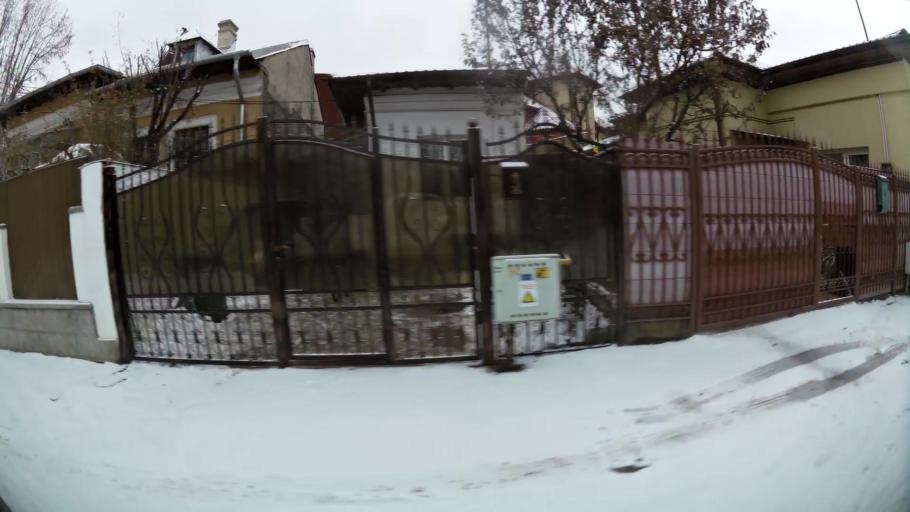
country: RO
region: Prahova
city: Ploiesti
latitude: 44.9376
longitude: 26.0338
